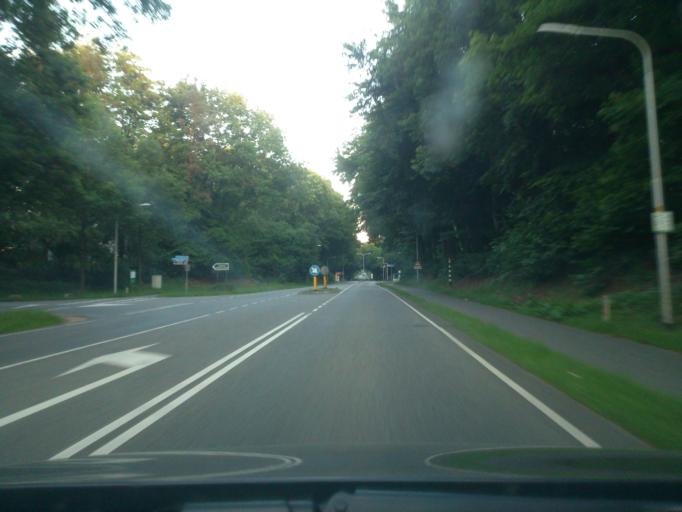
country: NL
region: Gelderland
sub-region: Gemeente Groesbeek
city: Berg en Dal
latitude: 51.7973
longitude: 5.9057
